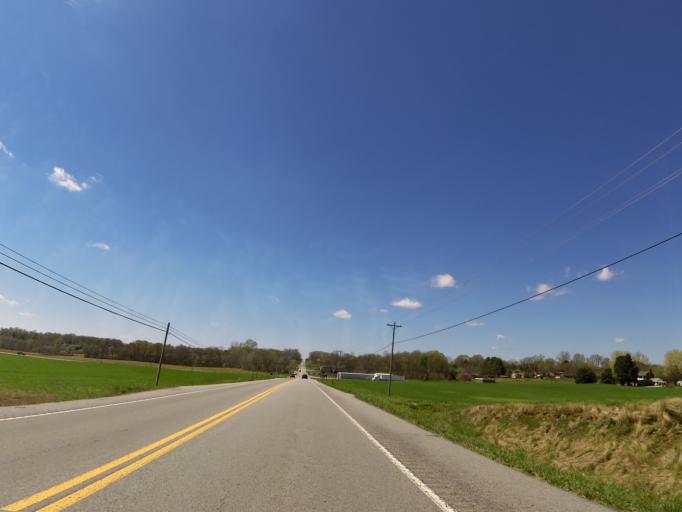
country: US
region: Tennessee
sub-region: White County
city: Sparta
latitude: 35.9538
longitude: -85.5677
